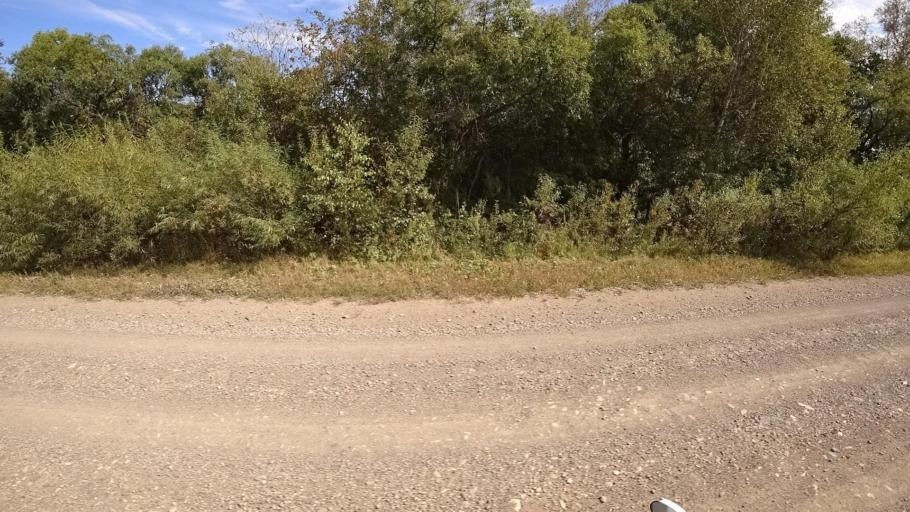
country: RU
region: Primorskiy
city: Yakovlevka
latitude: 44.7206
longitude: 133.6150
